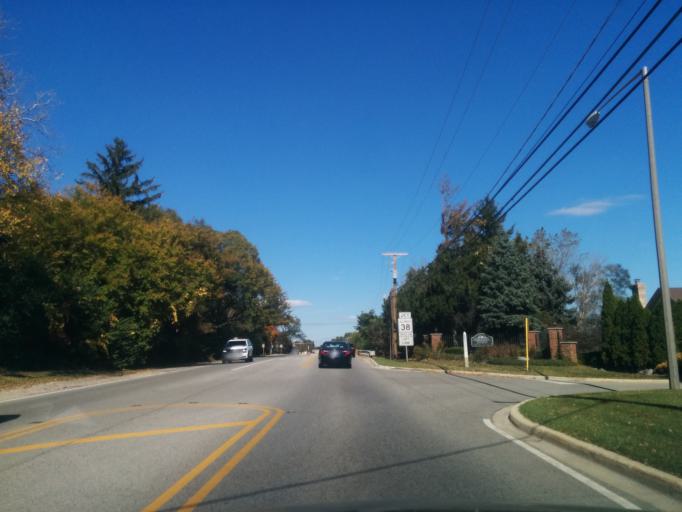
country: US
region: Illinois
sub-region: DuPage County
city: Glen Ellyn
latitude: 41.8548
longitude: -88.0527
